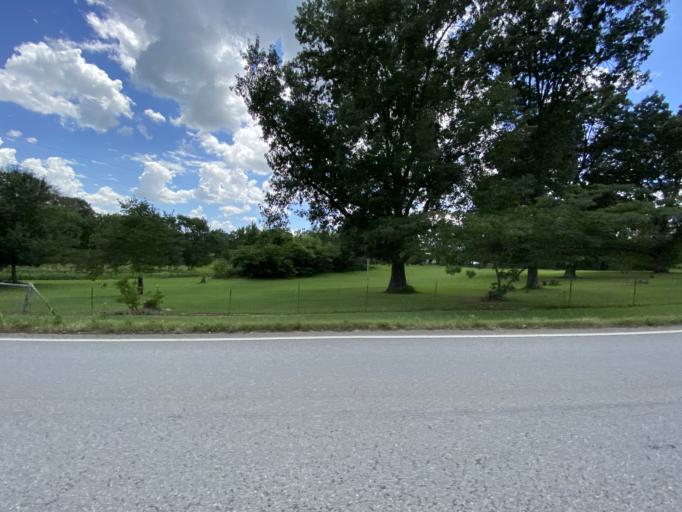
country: US
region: Alabama
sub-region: Lauderdale County
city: Underwood-Petersville
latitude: 34.9447
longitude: -87.8612
